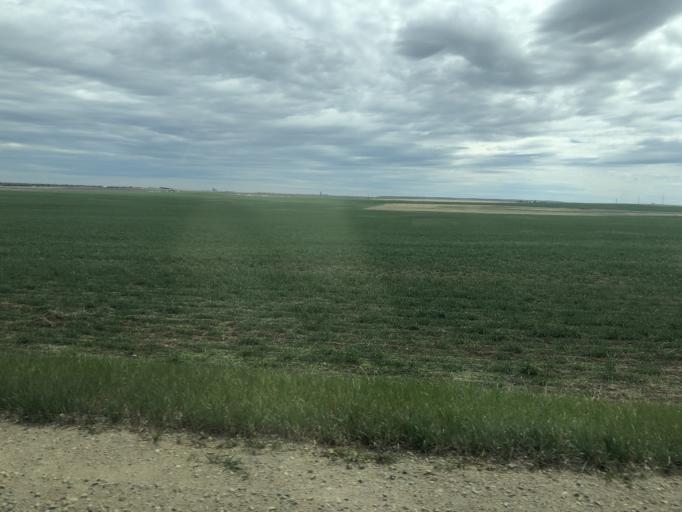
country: CA
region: Alberta
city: Vulcan
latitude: 50.3736
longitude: -113.3231
